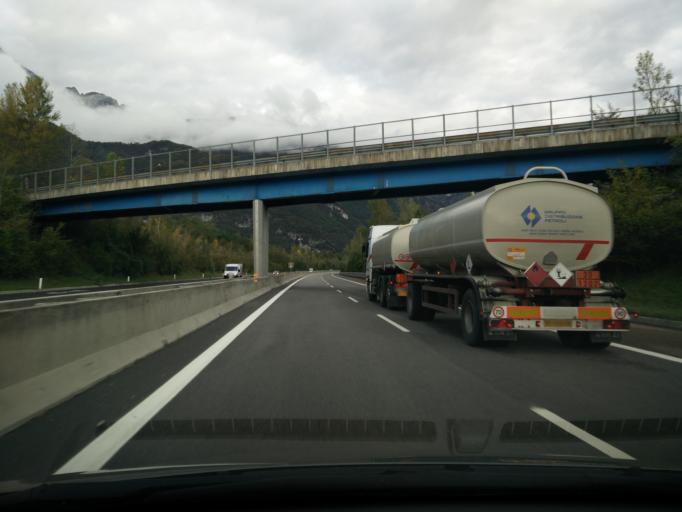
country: IT
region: Veneto
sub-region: Provincia di Belluno
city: Ponte nell'Alpi
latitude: 46.1816
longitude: 12.2951
